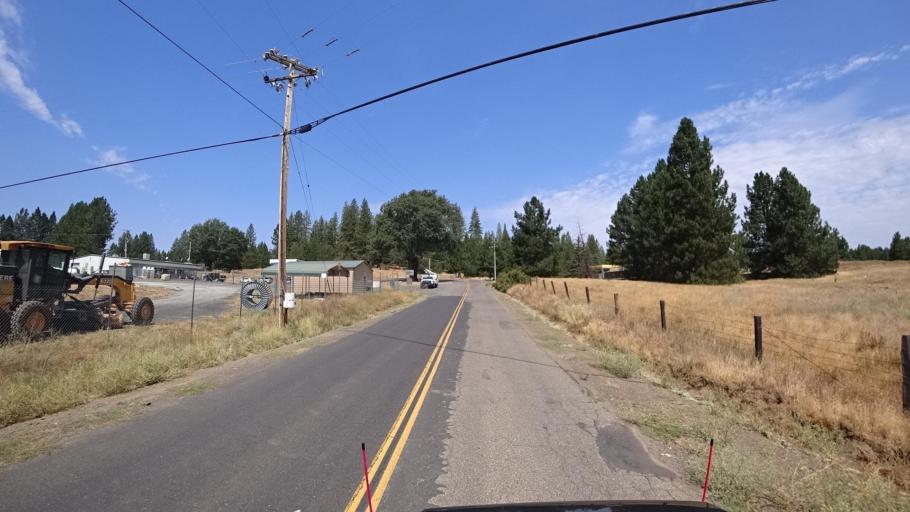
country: US
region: California
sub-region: Tuolumne County
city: Tuolumne City
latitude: 37.7405
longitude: -120.1313
